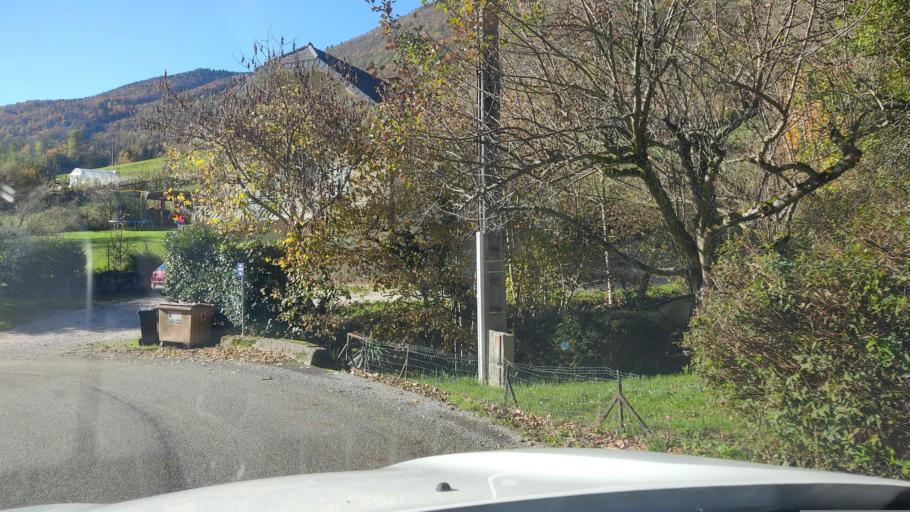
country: FR
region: Rhone-Alpes
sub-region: Departement de la Savoie
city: Vimines
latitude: 45.5050
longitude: 5.8409
